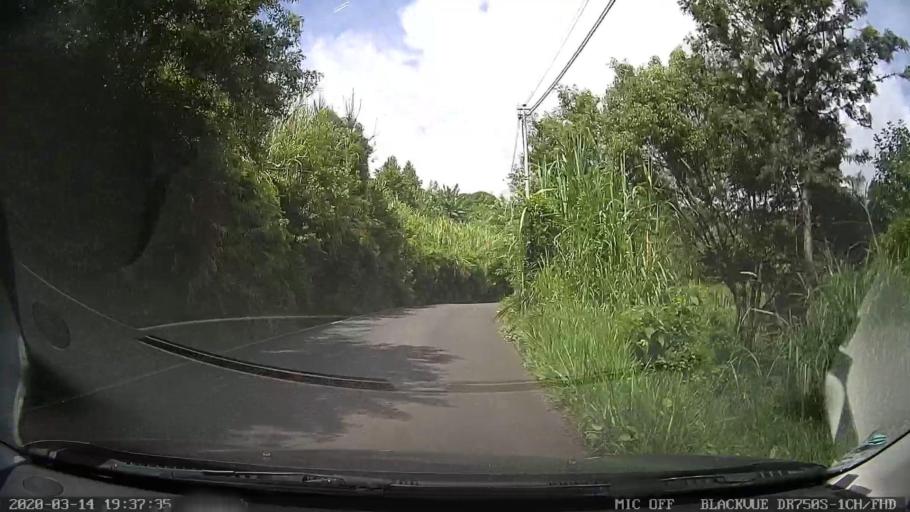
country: RE
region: Reunion
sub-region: Reunion
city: Sainte-Marie
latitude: -20.9438
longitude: 55.5222
